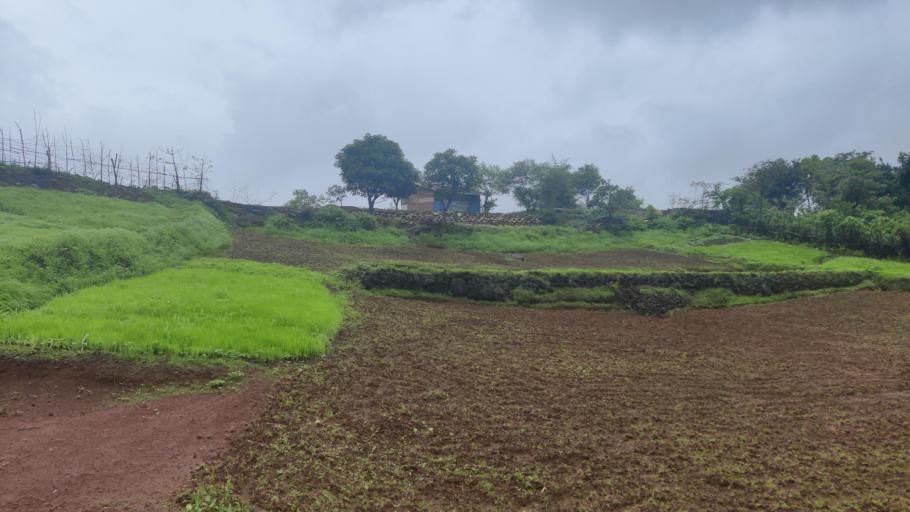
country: IN
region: Maharashtra
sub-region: Thane
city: Thane
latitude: 19.2408
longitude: 72.9608
